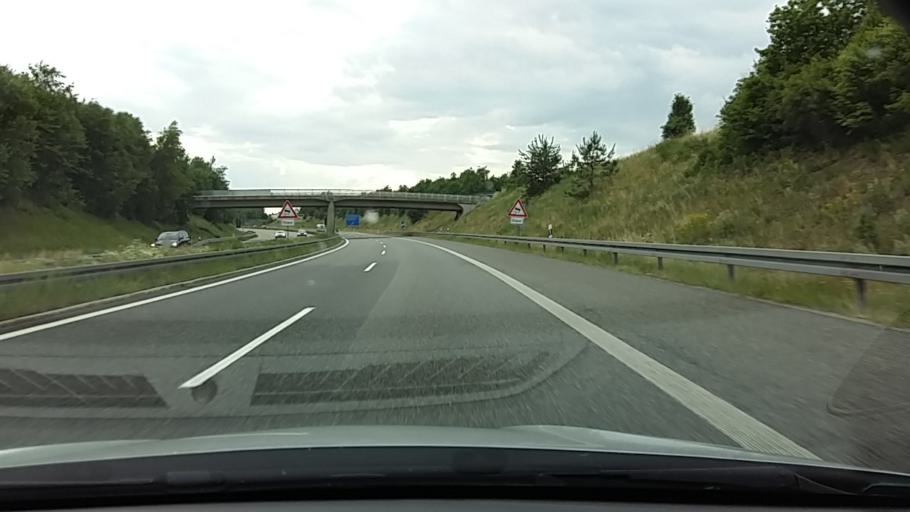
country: DE
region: Bavaria
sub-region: Upper Palatinate
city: Vohenstrauss
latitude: 49.6188
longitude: 12.3591
